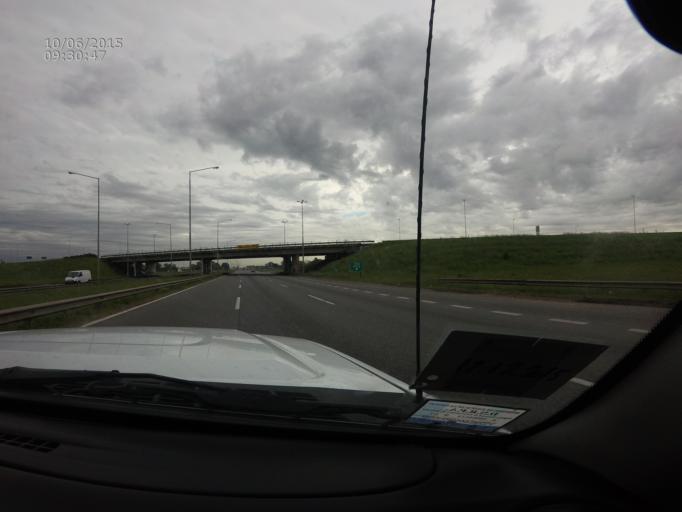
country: AR
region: Buenos Aires
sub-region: Partido de Zarate
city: Zarate
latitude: -34.1389
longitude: -59.0515
